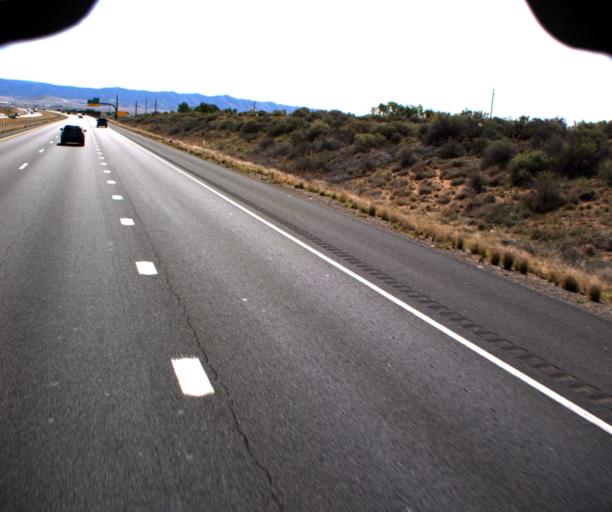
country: US
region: Arizona
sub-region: Yavapai County
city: Prescott Valley
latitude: 34.6343
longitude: -112.3434
